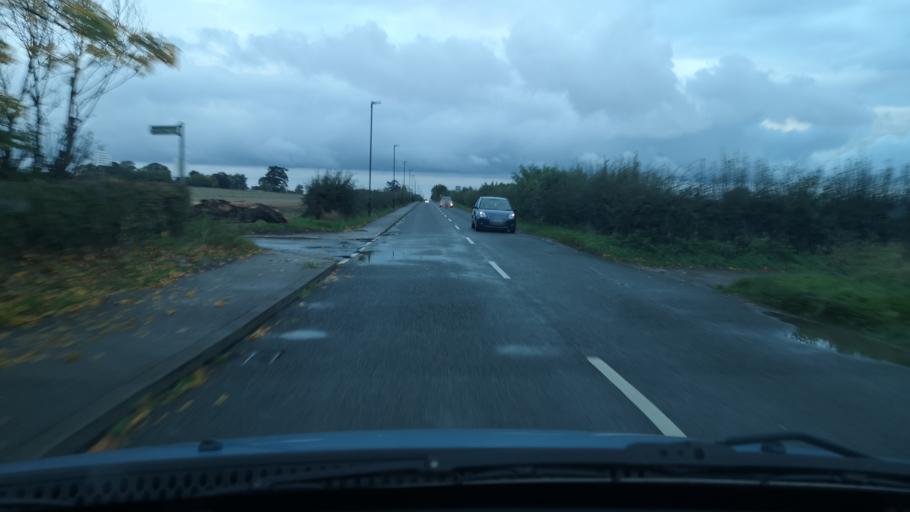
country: GB
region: England
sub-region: Doncaster
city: Norton
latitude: 53.6266
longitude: -1.1820
